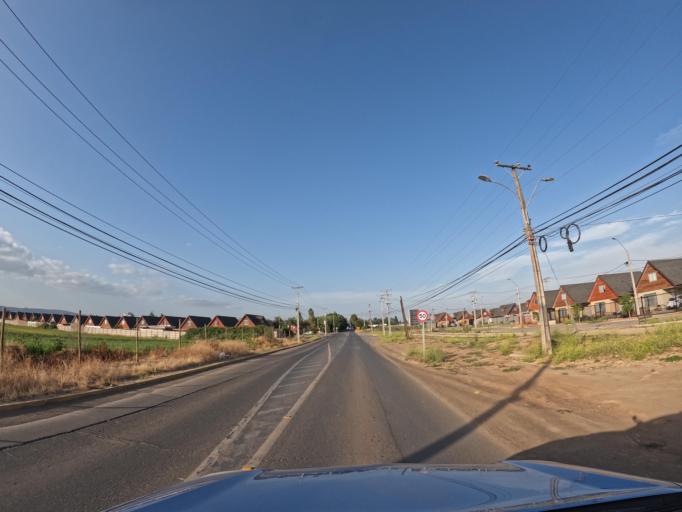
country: CL
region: Maule
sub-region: Provincia de Talca
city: Talca
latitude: -35.4462
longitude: -71.6170
